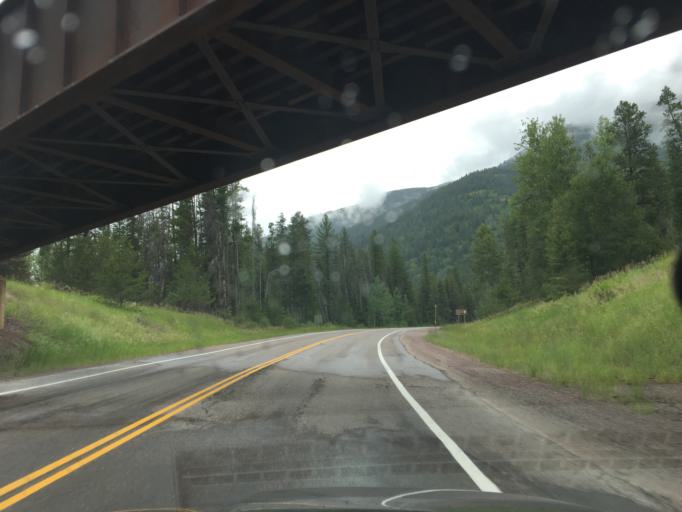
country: US
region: Montana
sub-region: Flathead County
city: Bigfork
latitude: 48.2390
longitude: -113.5693
